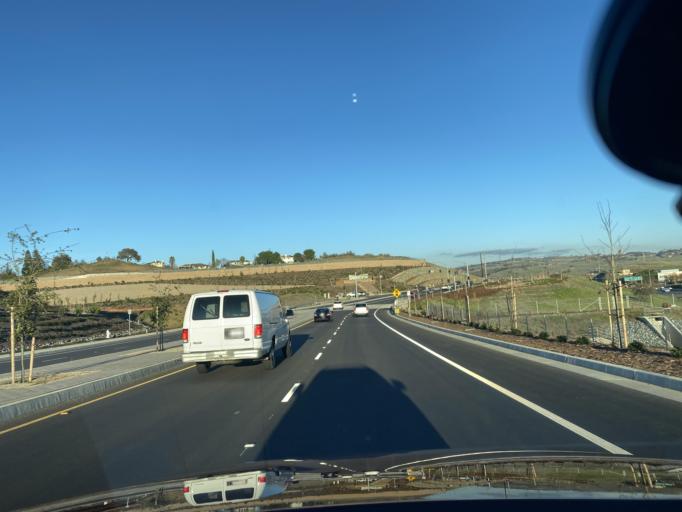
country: US
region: California
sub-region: El Dorado County
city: El Dorado Hills
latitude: 38.6499
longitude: -121.0821
